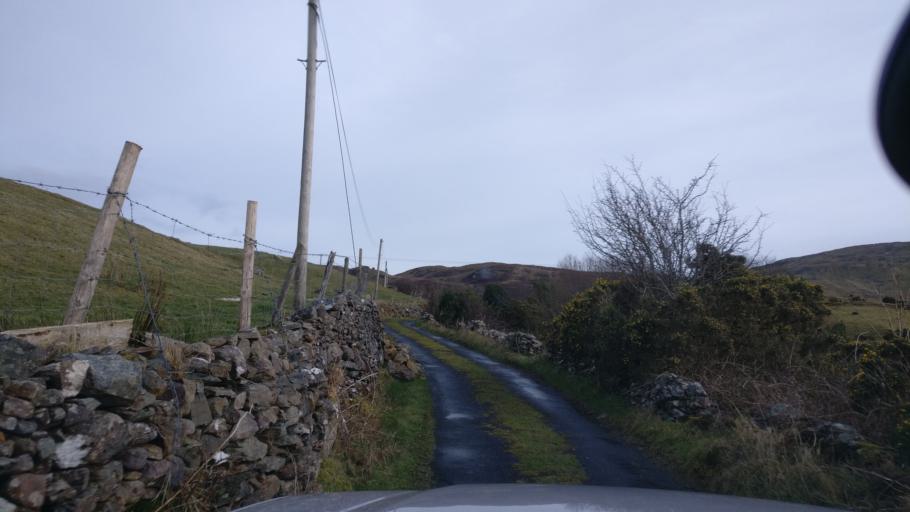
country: IE
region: Connaught
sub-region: County Galway
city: Oughterard
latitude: 53.5533
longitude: -9.4414
